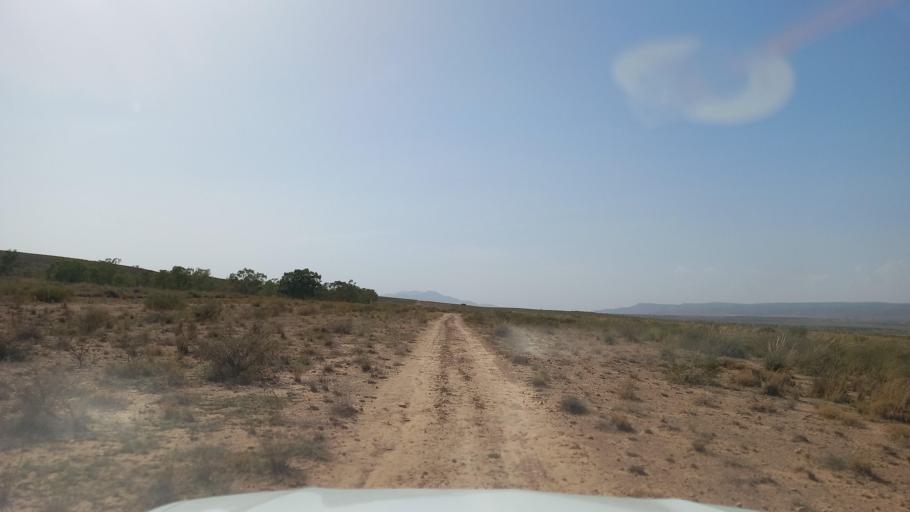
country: TN
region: Al Qasrayn
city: Kasserine
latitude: 35.2142
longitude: 8.9978
